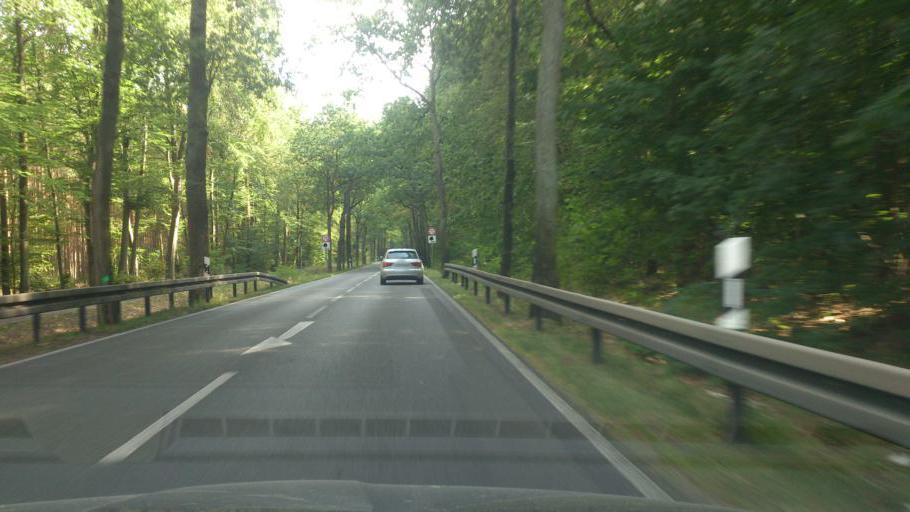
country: DE
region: Berlin
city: Wannsee
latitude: 52.3499
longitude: 13.1495
